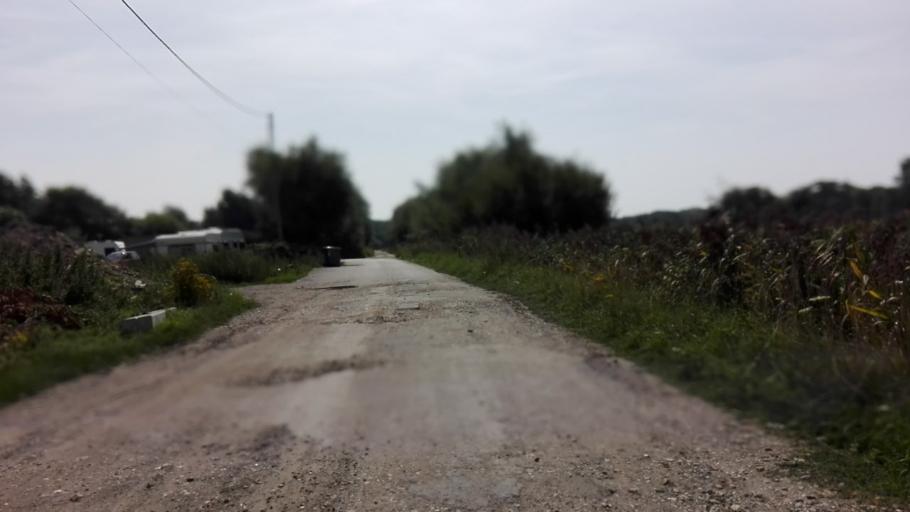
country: FR
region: Nord-Pas-de-Calais
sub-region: Departement du Pas-de-Calais
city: Berck
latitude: 50.3986
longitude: 1.5821
